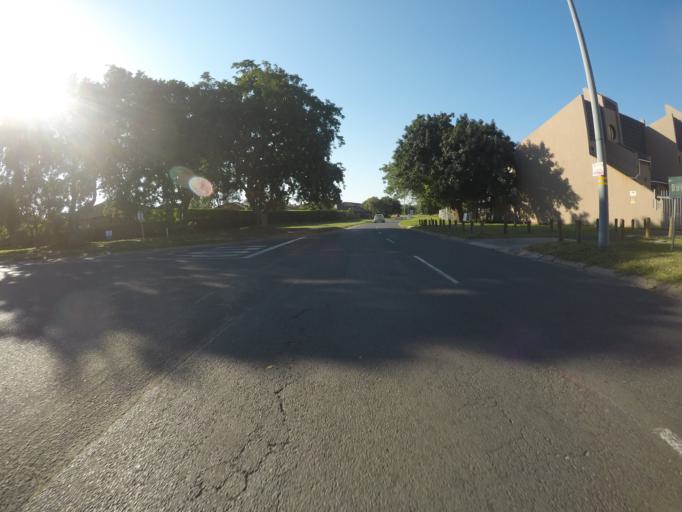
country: ZA
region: KwaZulu-Natal
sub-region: uThungulu District Municipality
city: Richards Bay
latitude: -28.7929
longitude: 32.0974
